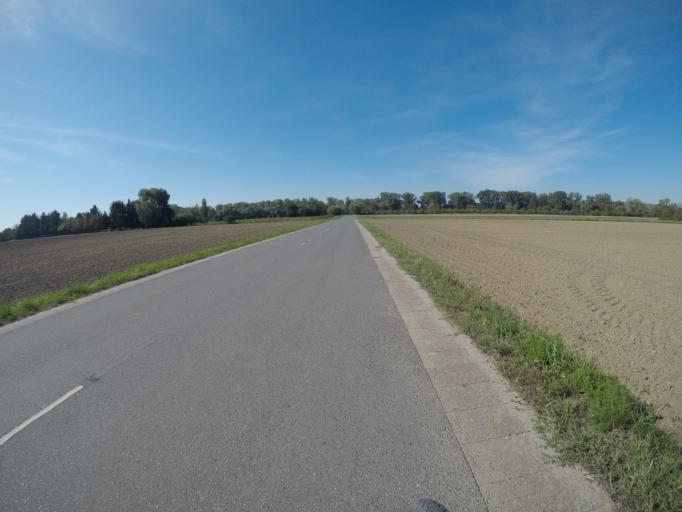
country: DE
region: Rheinland-Pfalz
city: Eich
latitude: 49.7771
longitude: 8.4269
